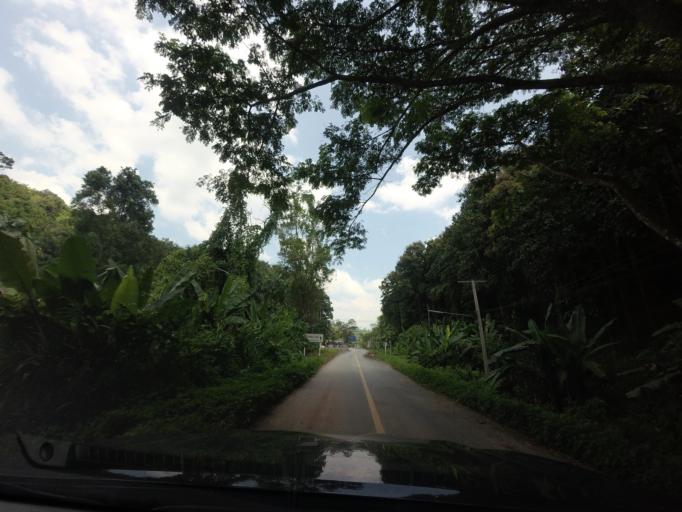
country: TH
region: Loei
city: Na Haeo
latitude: 17.6394
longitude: 100.9064
